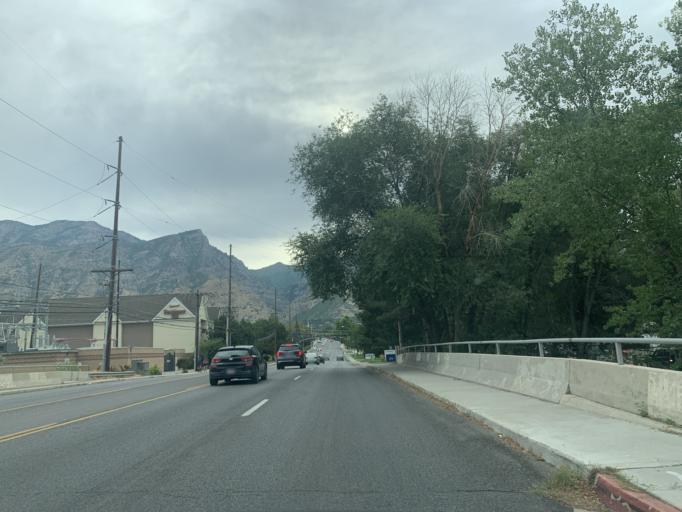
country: US
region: Utah
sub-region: Utah County
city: Provo
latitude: 40.2635
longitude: -111.6642
